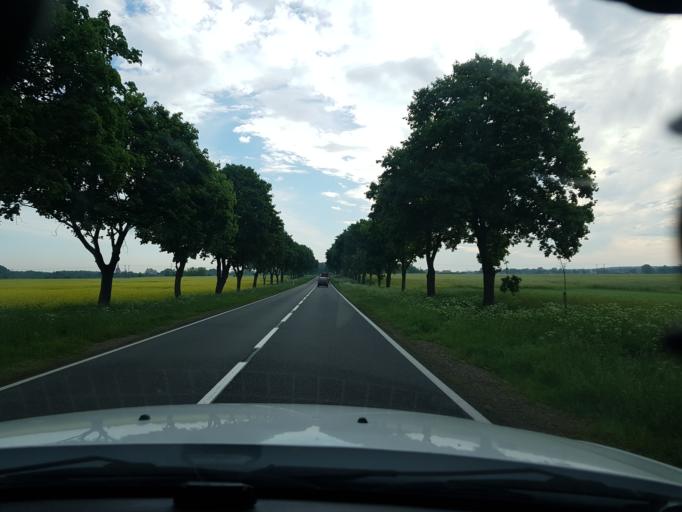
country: PL
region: West Pomeranian Voivodeship
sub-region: Powiat stargardzki
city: Chociwel
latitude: 53.4520
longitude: 15.3203
